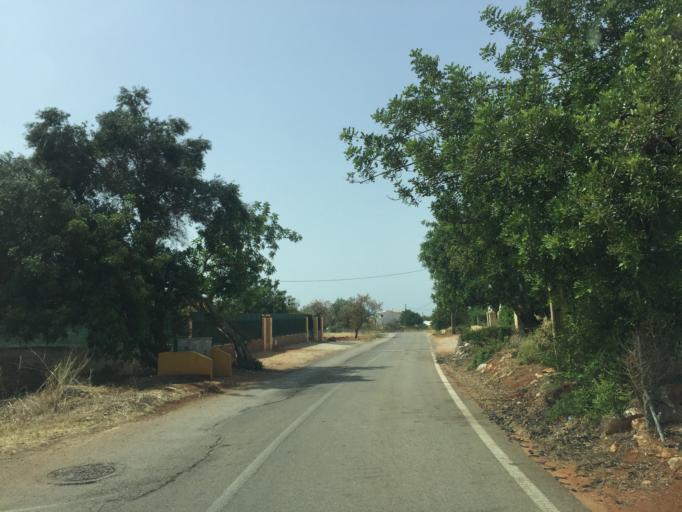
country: PT
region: Faro
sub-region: Loule
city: Boliqueime
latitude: 37.1311
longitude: -8.1414
